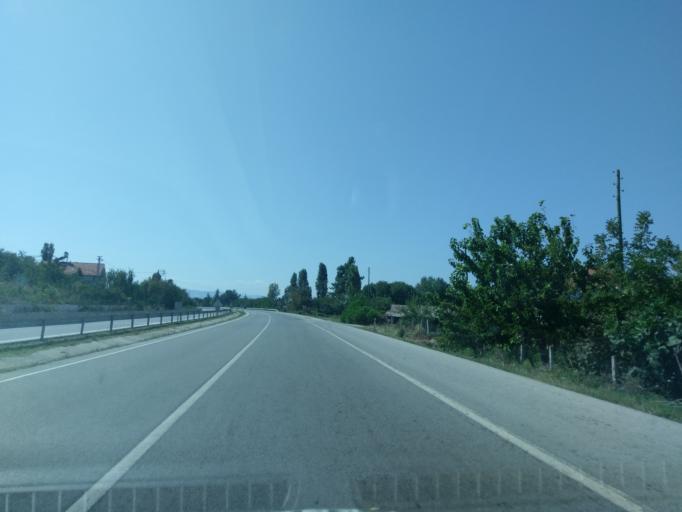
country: TR
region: Samsun
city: Alacam
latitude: 41.6125
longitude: 35.7092
